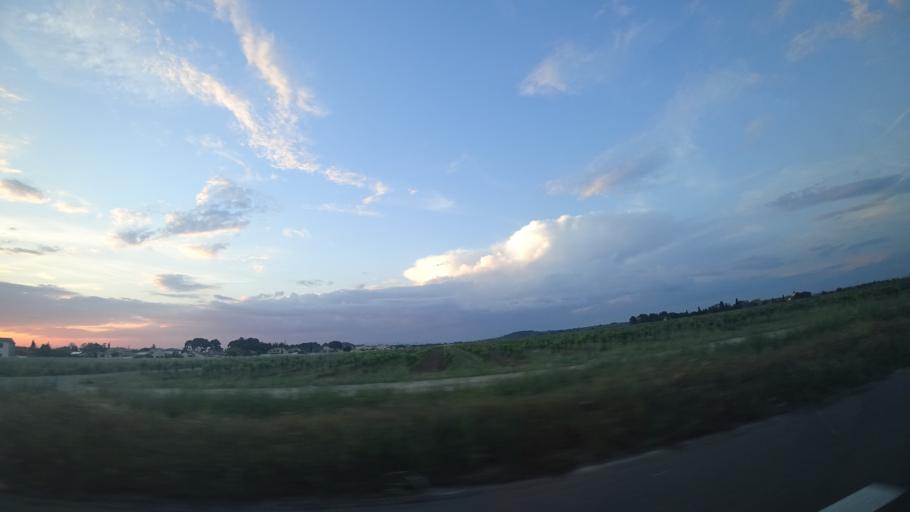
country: FR
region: Languedoc-Roussillon
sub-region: Departement de l'Herault
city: Montady
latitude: 43.3333
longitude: 3.1407
